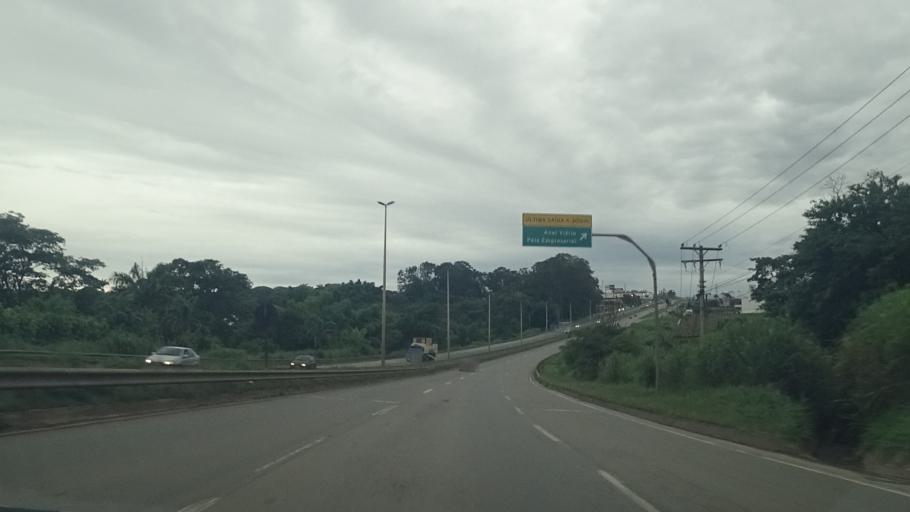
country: BR
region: Goias
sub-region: Aparecida De Goiania
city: Aparecida de Goiania
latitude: -16.7751
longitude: -49.2372
